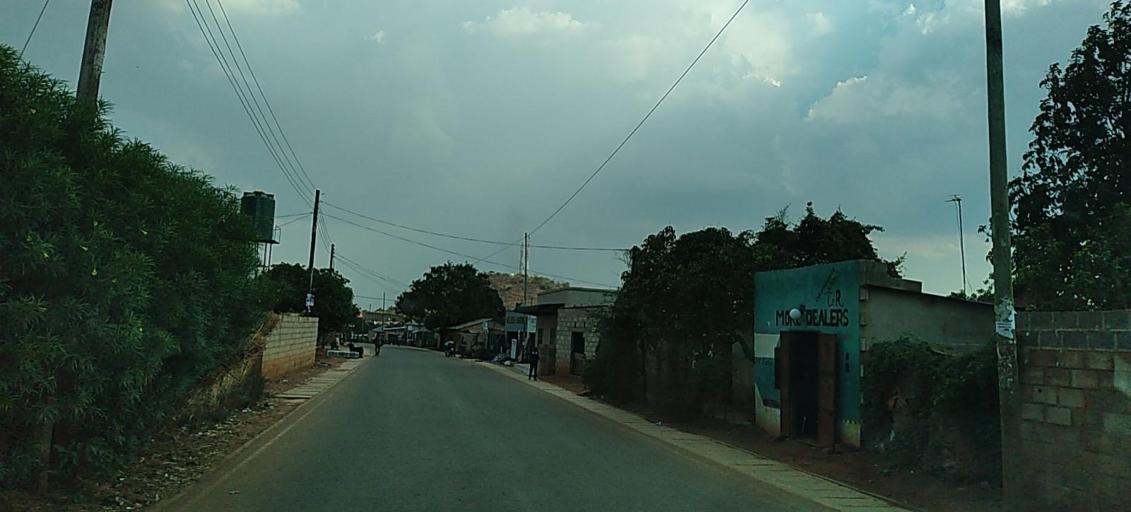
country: ZM
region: Lusaka
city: Lusaka
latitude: -15.5361
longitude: 28.2375
